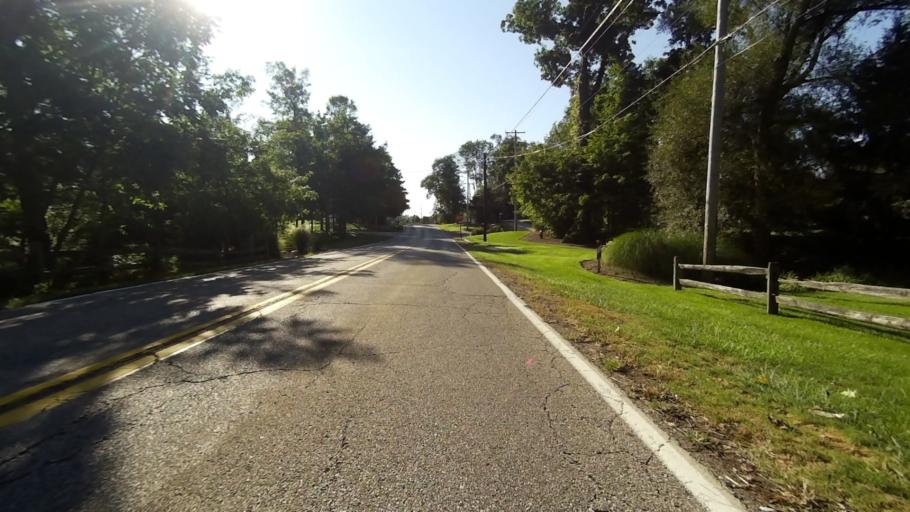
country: US
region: Ohio
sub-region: Portage County
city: Aurora
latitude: 41.3071
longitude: -81.3304
